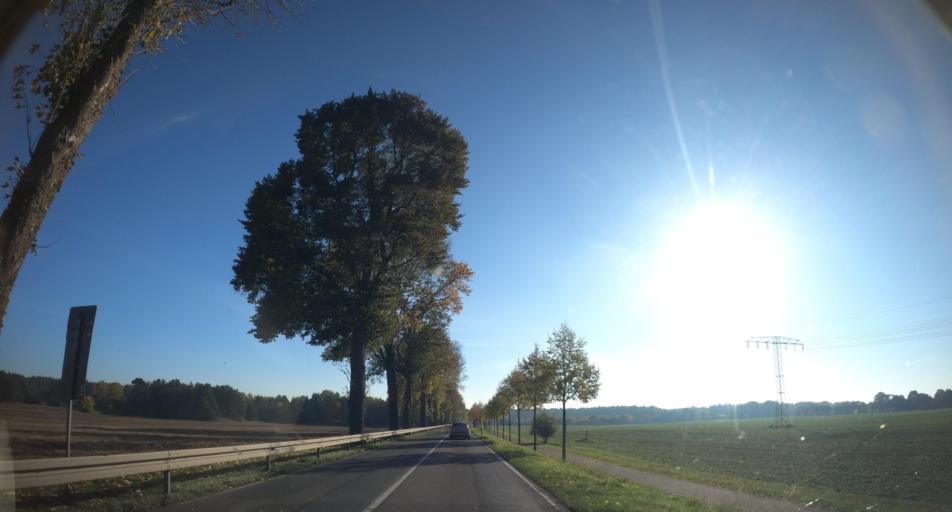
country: DE
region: Mecklenburg-Vorpommern
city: Ueckermunde
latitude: 53.7198
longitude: 14.0633
